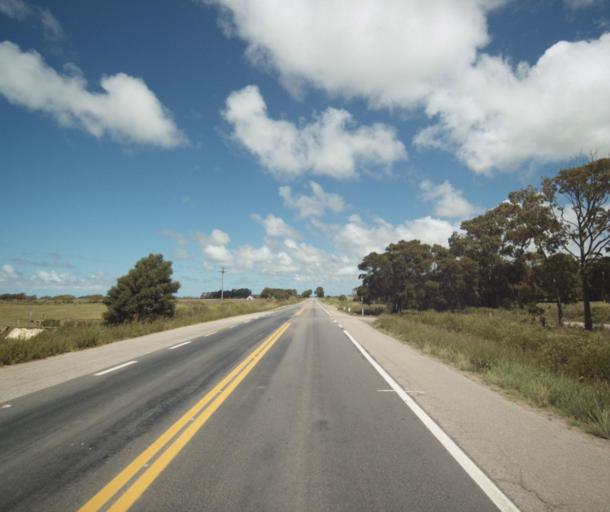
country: UY
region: Cerro Largo
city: Rio Branco
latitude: -32.8840
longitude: -52.7205
